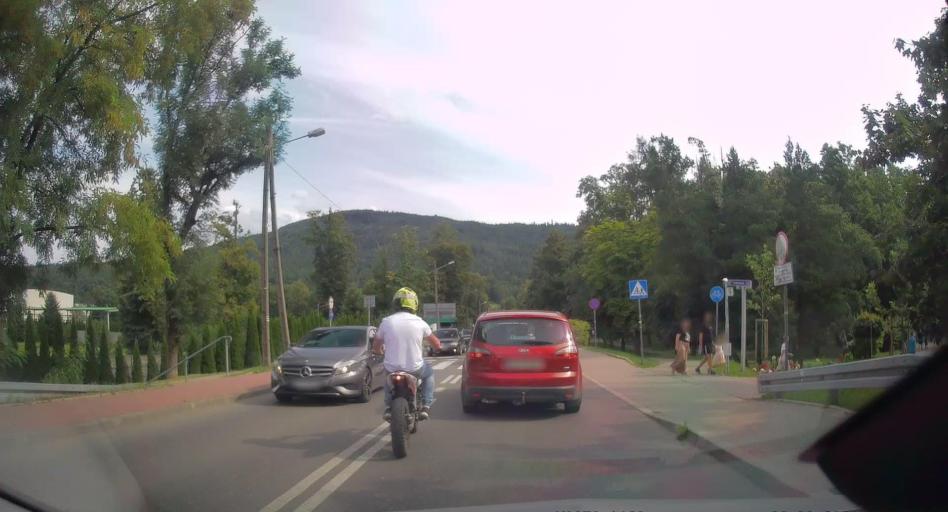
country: PL
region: Lesser Poland Voivodeship
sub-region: Powiat myslenicki
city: Myslenice
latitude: 49.8235
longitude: 19.9454
